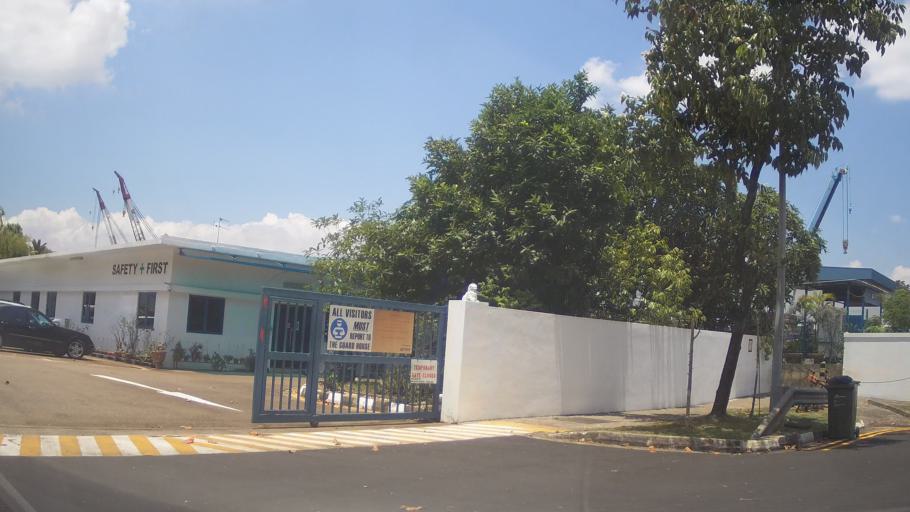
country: SG
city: Singapore
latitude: 1.3050
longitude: 103.6738
